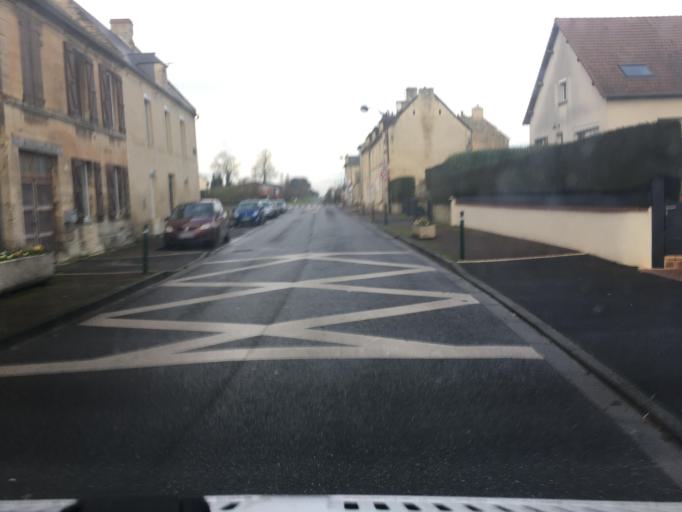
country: FR
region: Lower Normandy
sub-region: Departement du Calvados
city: Saint-Manvieu
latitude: 49.2130
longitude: -0.5204
